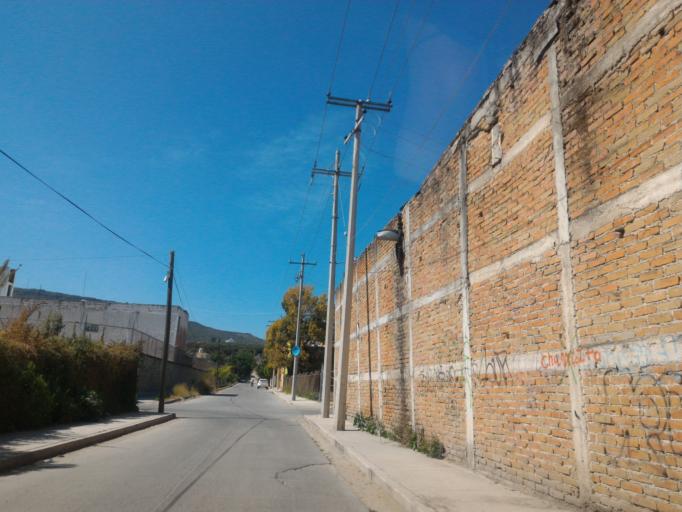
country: MX
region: Guanajuato
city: San Francisco del Rincon
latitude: 21.0328
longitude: -101.8833
